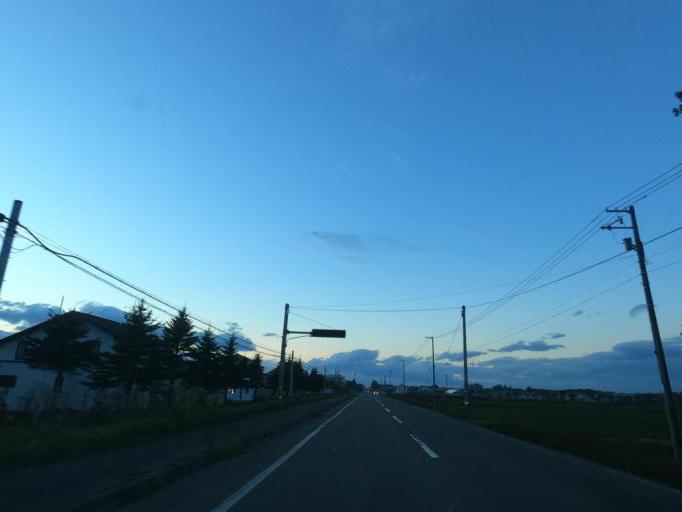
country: JP
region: Hokkaido
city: Obihiro
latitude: 42.6477
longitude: 143.1959
